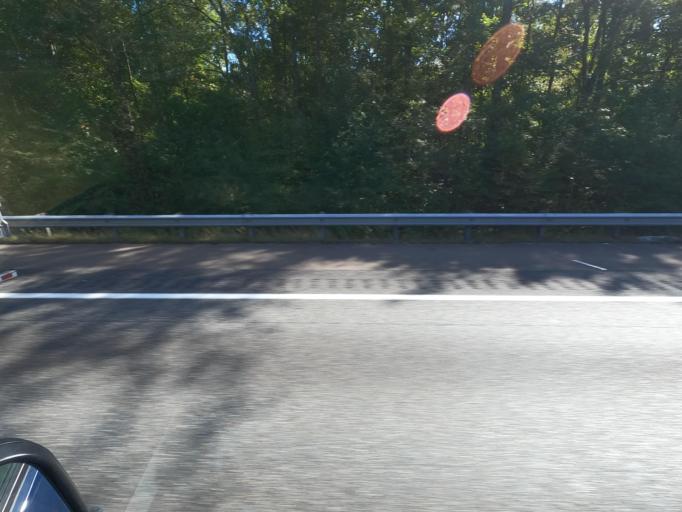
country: US
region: Tennessee
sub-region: Haywood County
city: Brownsville
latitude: 35.5069
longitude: -89.2652
